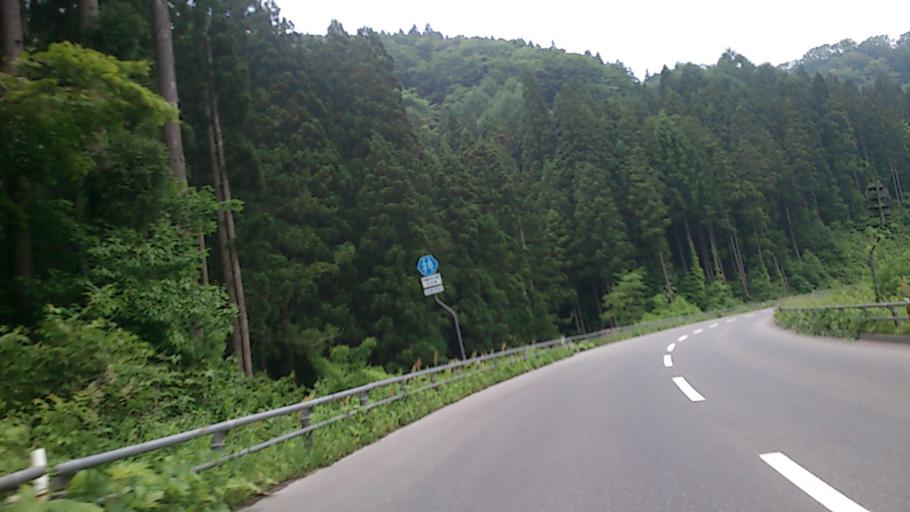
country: JP
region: Aomori
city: Hirosaki
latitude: 40.5308
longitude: 140.2672
